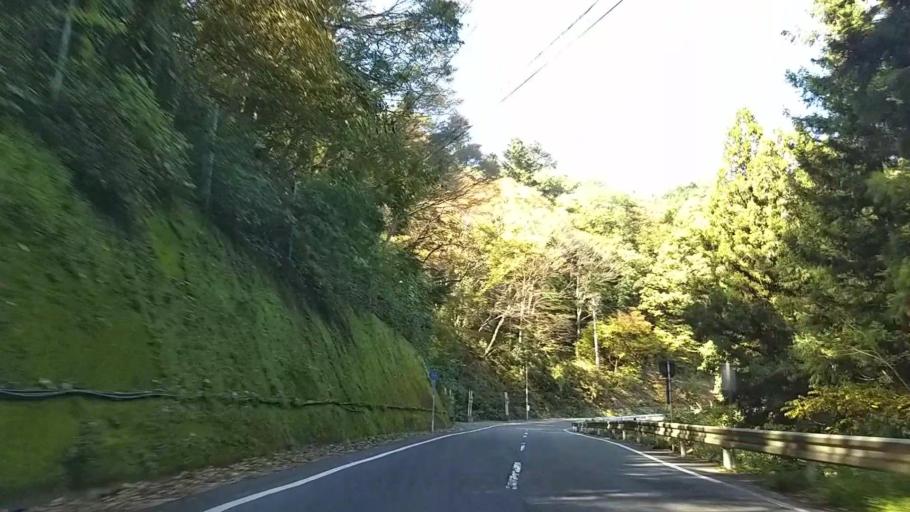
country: JP
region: Yamanashi
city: Uenohara
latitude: 35.6453
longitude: 139.0970
